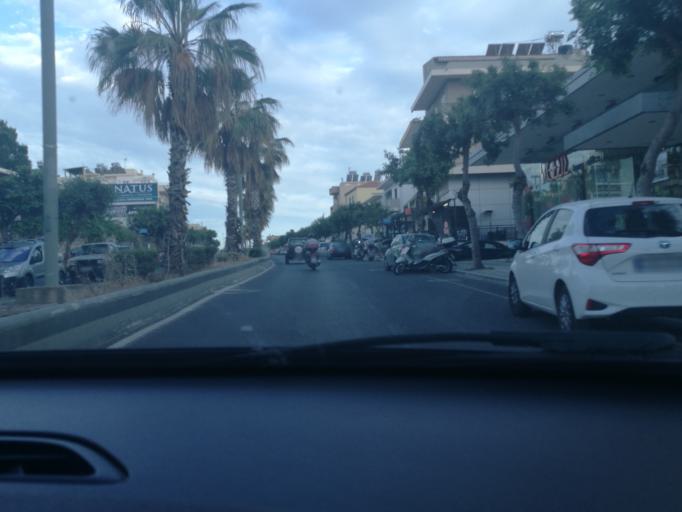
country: GR
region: Crete
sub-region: Nomos Irakleiou
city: Irakleion
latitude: 35.3179
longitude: 25.1451
